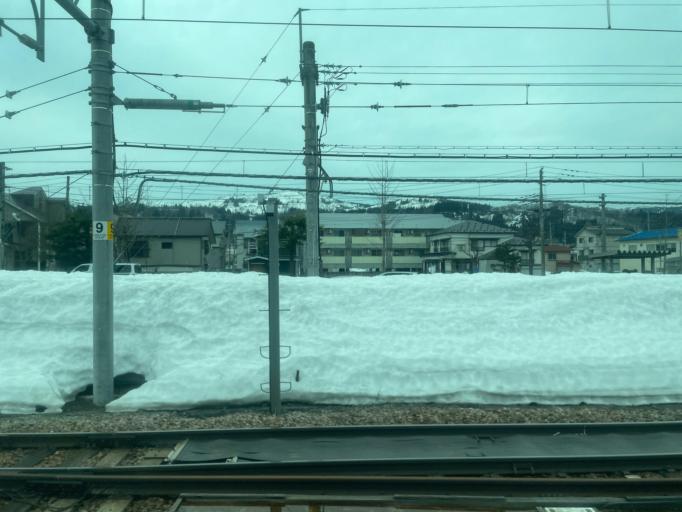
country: JP
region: Niigata
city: Muikamachi
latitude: 37.0644
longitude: 138.8740
